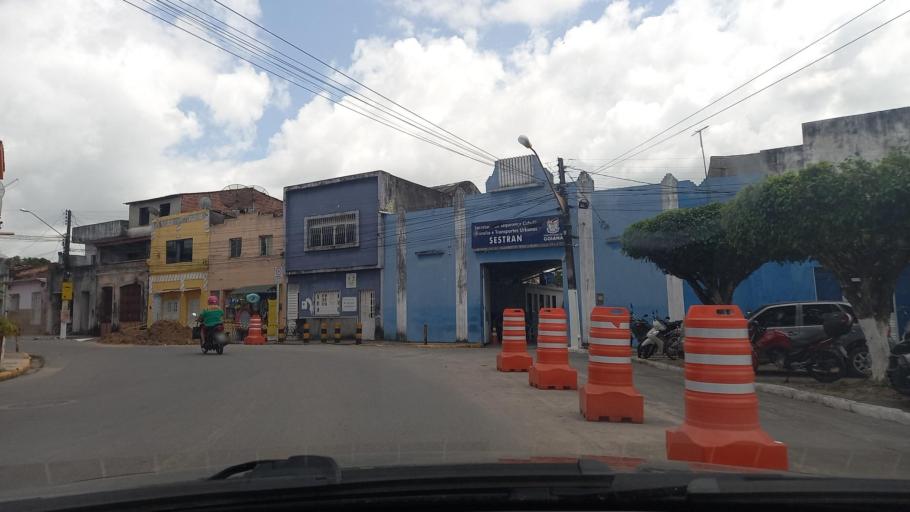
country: BR
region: Pernambuco
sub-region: Goiana
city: Goiana
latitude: -7.5571
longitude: -35.0005
